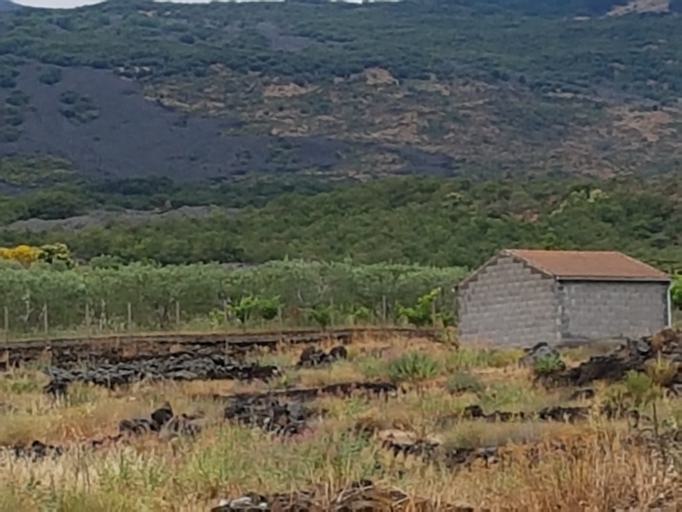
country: IT
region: Sicily
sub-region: Catania
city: Randazzo
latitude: 37.8697
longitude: 14.9797
